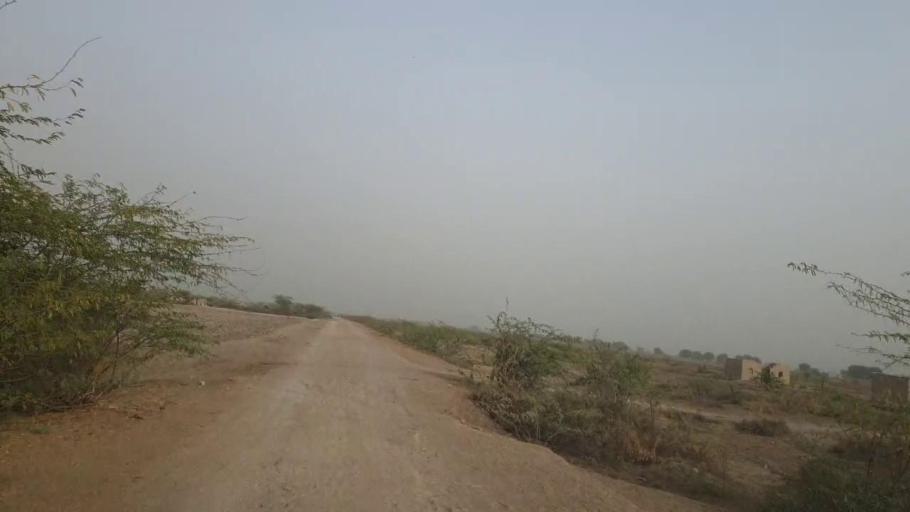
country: PK
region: Sindh
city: Kunri
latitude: 25.0968
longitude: 69.4481
